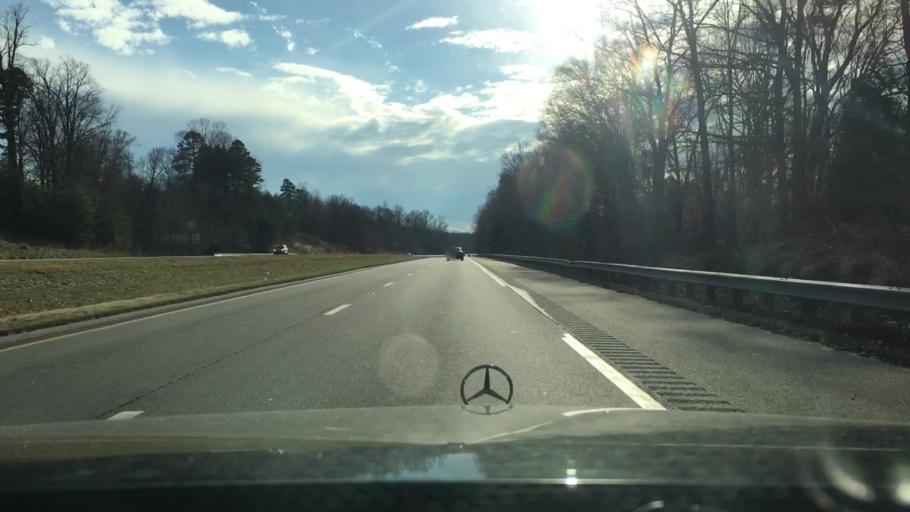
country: US
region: Virginia
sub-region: City of Danville
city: Danville
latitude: 36.5536
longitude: -79.3911
